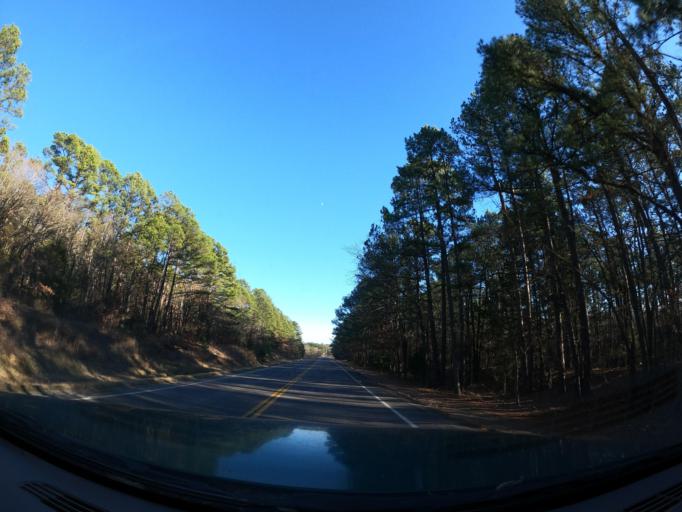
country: US
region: Oklahoma
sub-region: Latimer County
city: Wilburton
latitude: 34.9596
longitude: -95.3514
